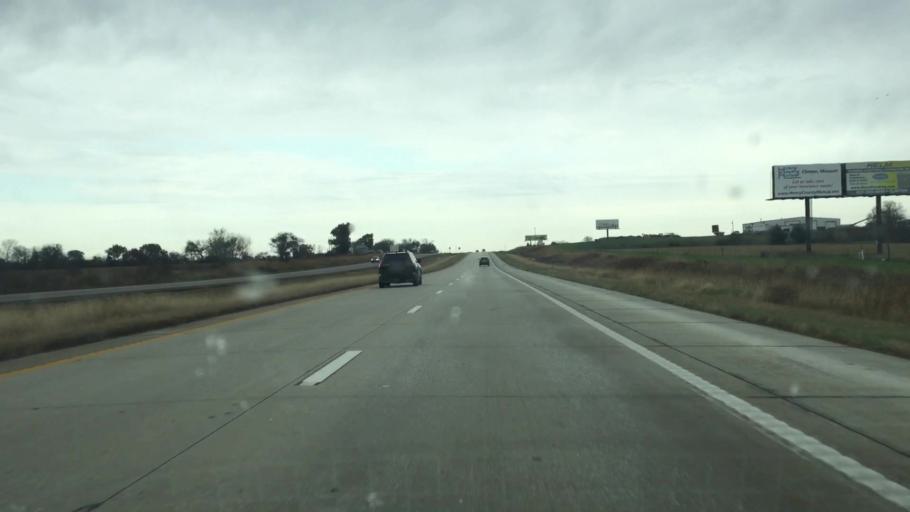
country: US
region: Missouri
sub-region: Saint Clair County
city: Osceola
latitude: 38.1622
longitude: -93.7220
